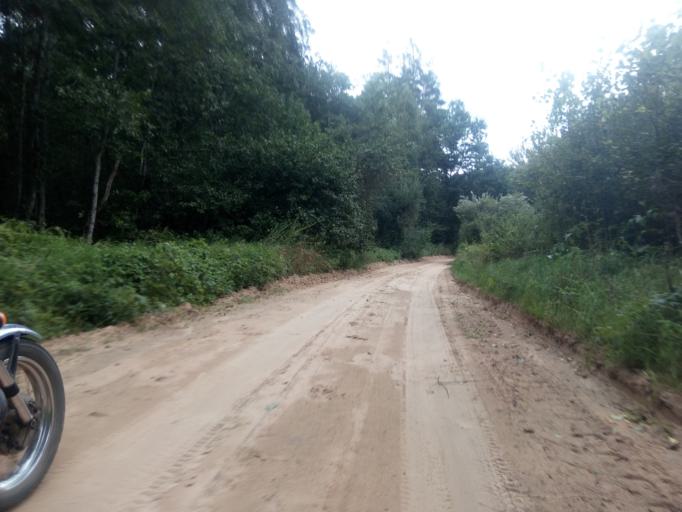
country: BY
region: Vitebsk
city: Dzisna
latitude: 55.7055
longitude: 28.3330
